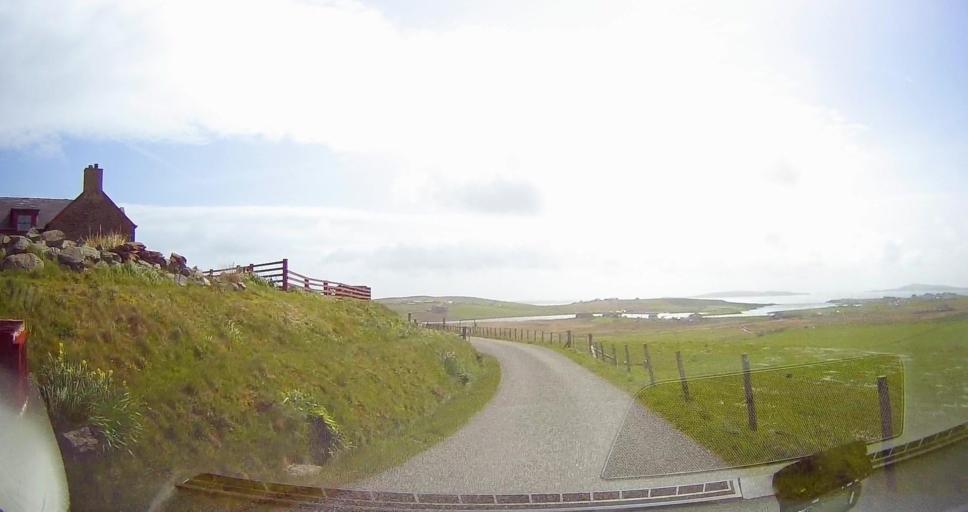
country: GB
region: Scotland
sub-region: Shetland Islands
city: Sandwick
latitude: 60.0501
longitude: -1.2211
